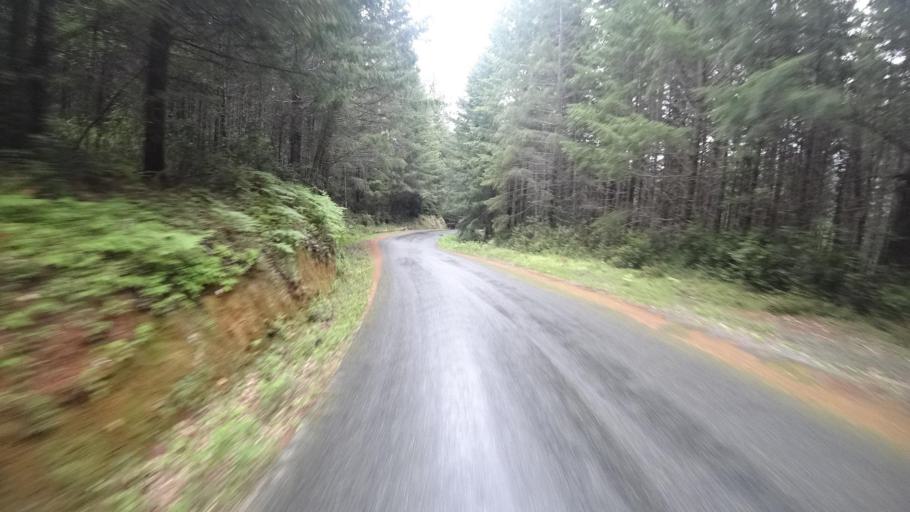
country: US
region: California
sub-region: Humboldt County
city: Willow Creek
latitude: 41.1998
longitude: -123.7618
